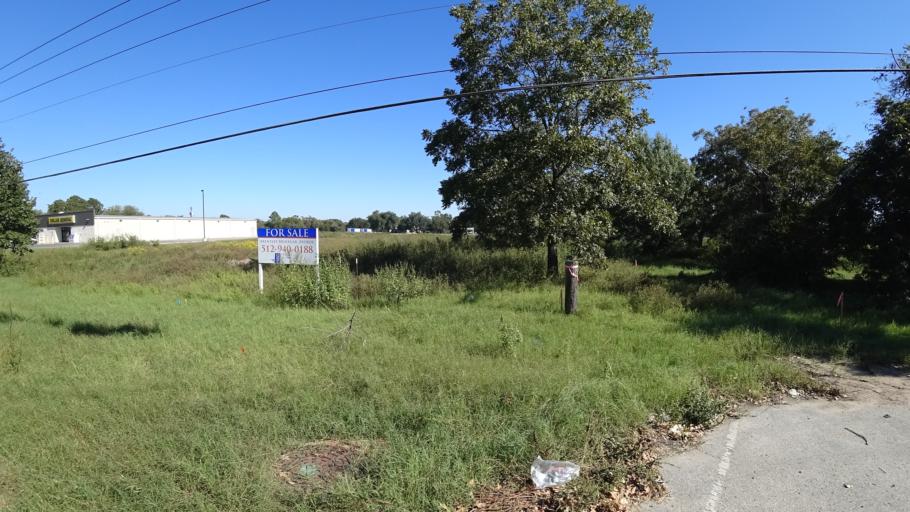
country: US
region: Texas
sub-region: Travis County
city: Hornsby Bend
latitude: 30.2495
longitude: -97.5874
